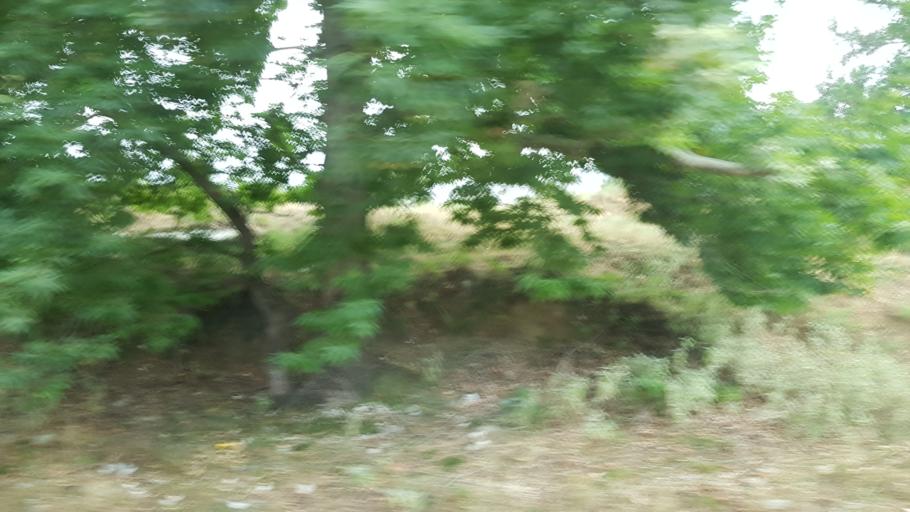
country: AL
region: Vlore
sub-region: Rrethi i Sarandes
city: Dhiver
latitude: 39.9133
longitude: 20.1884
